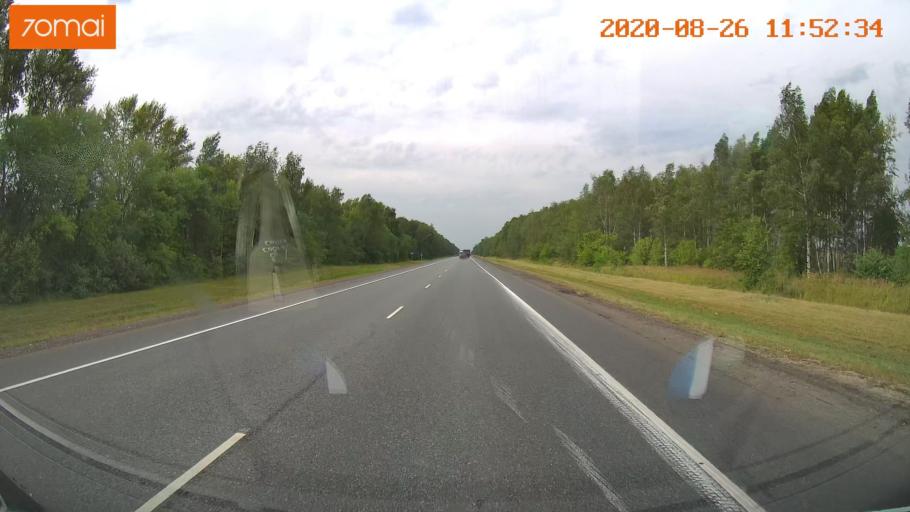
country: RU
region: Rjazan
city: Lesnoy
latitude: 54.2936
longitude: 40.4508
